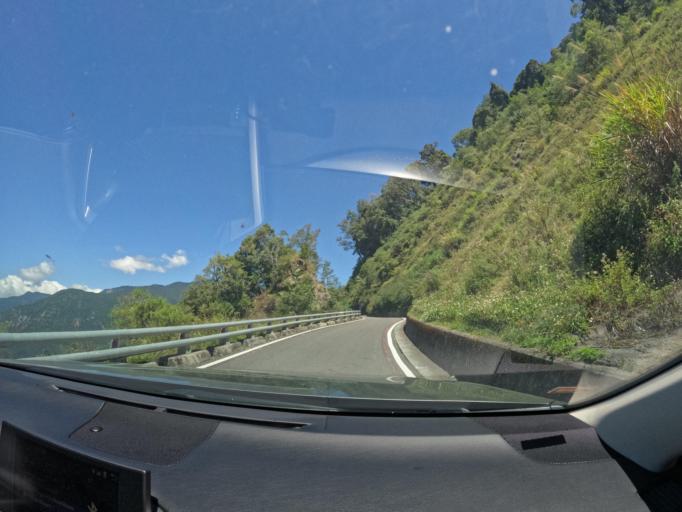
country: TW
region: Taiwan
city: Yujing
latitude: 23.2835
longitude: 120.8960
